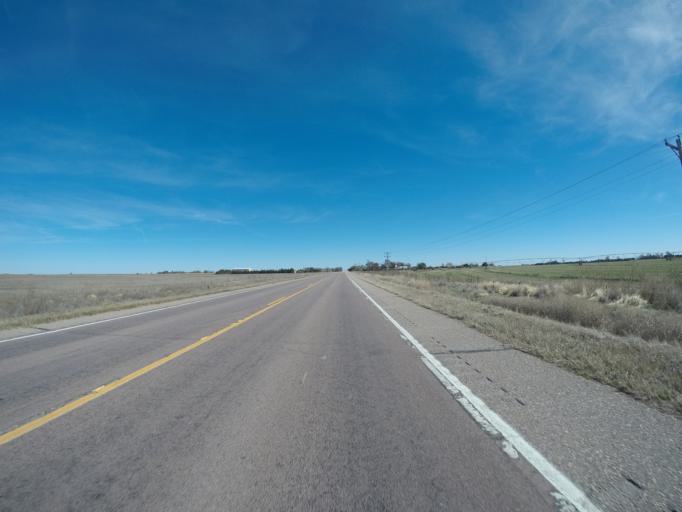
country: US
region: Colorado
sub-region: Yuma County
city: Yuma
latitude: 39.6560
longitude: -102.6928
